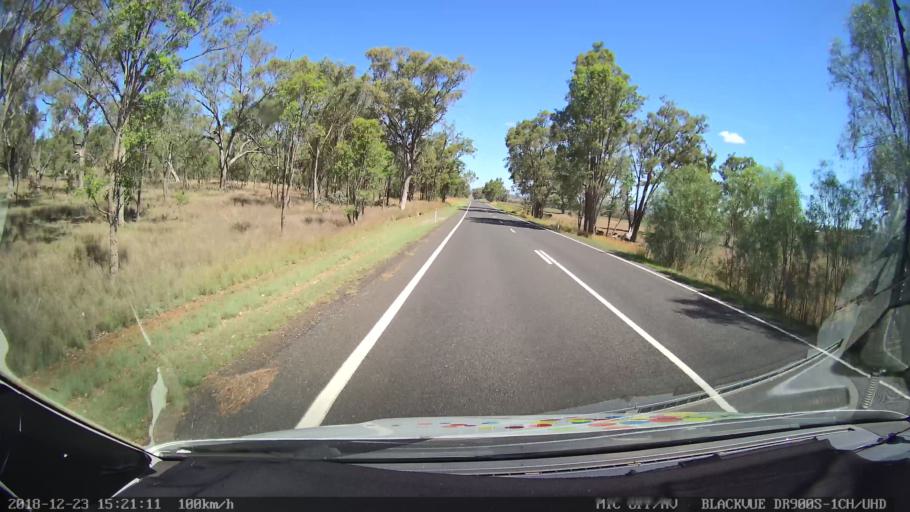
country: AU
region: New South Wales
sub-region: Tamworth Municipality
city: Manilla
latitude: -30.8528
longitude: 150.7948
